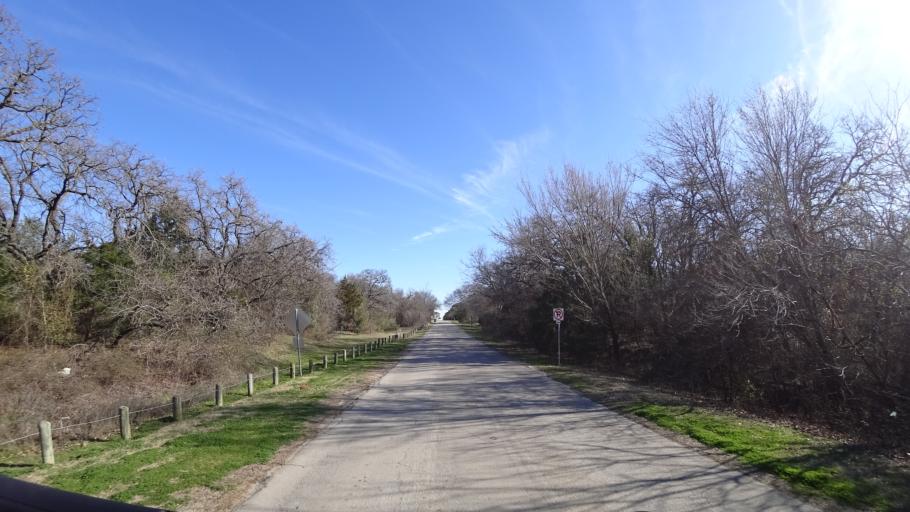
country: US
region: Texas
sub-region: Denton County
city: Highland Village
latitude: 33.0803
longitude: -97.0150
